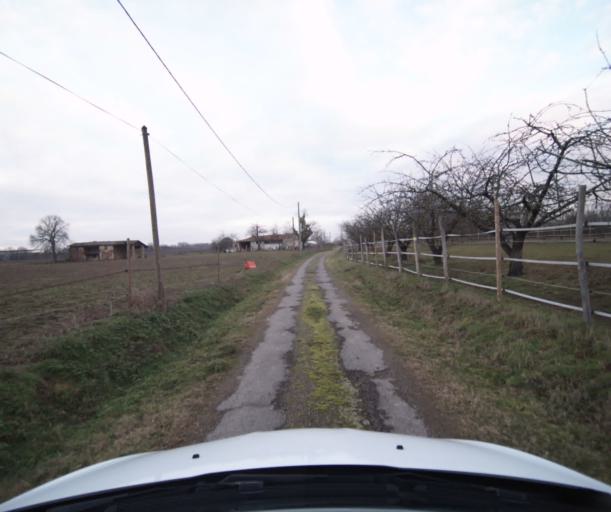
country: FR
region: Midi-Pyrenees
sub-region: Departement du Tarn-et-Garonne
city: Moissac
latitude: 44.0704
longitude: 1.1034
